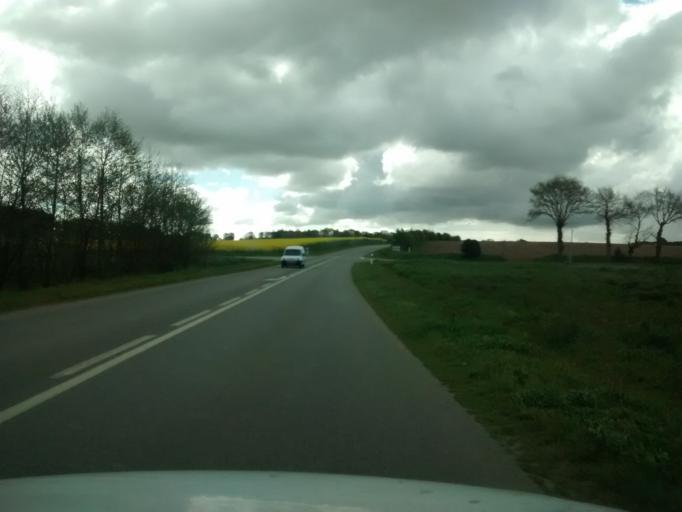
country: FR
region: Brittany
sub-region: Departement du Morbihan
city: Ruffiac
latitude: 47.8134
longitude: -2.2612
